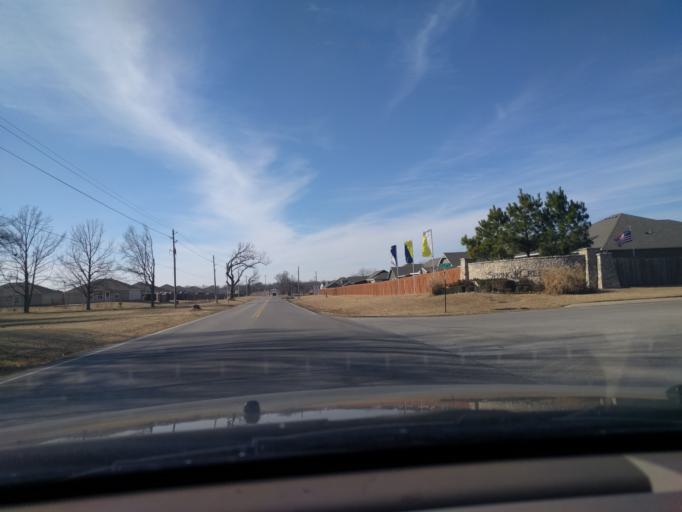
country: US
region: Oklahoma
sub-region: Wagoner County
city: Coweta
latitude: 36.0318
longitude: -95.6923
